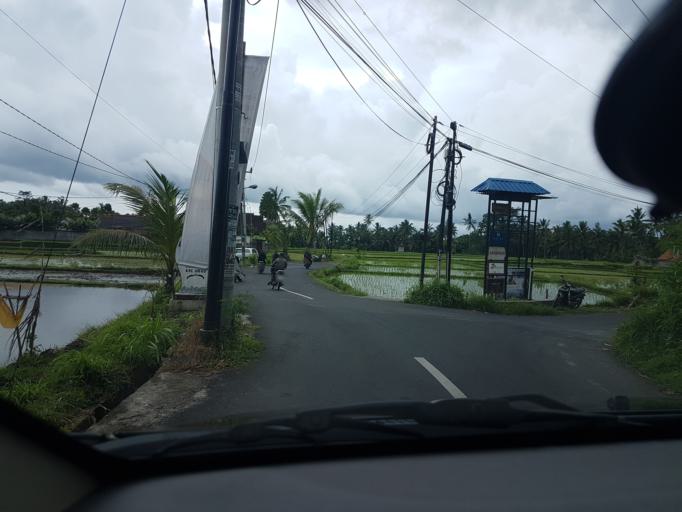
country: ID
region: Bali
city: Banjar Triwangsakeliki
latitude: -8.4680
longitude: 115.2714
